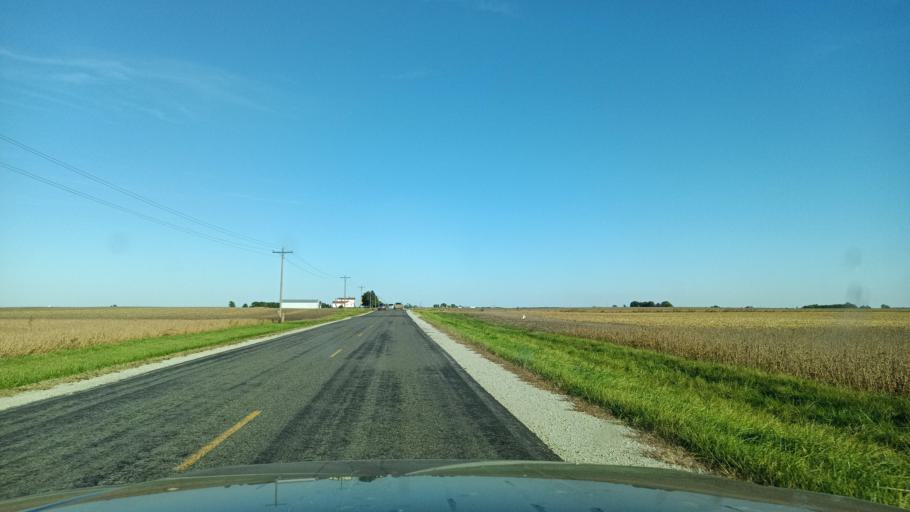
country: US
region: Illinois
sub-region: De Witt County
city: Farmer City
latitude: 40.2242
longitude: -88.7620
